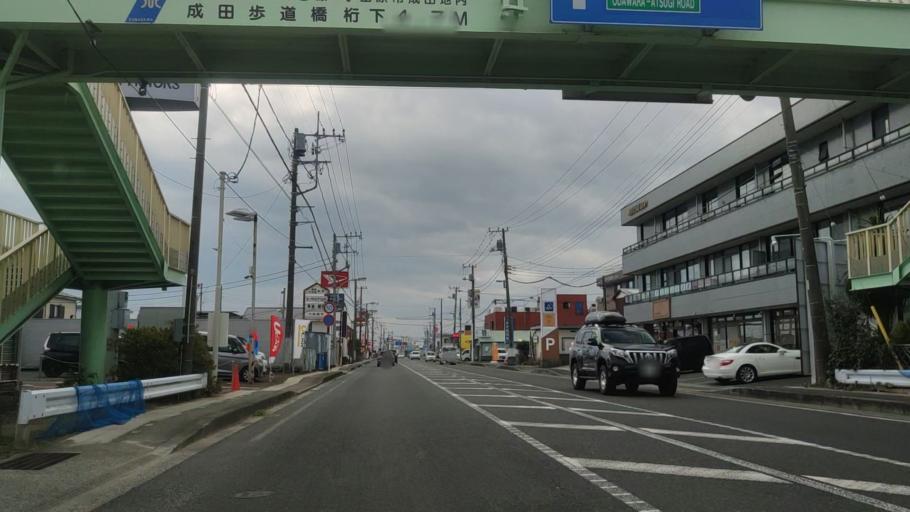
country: JP
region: Kanagawa
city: Odawara
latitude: 35.2959
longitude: 139.1673
